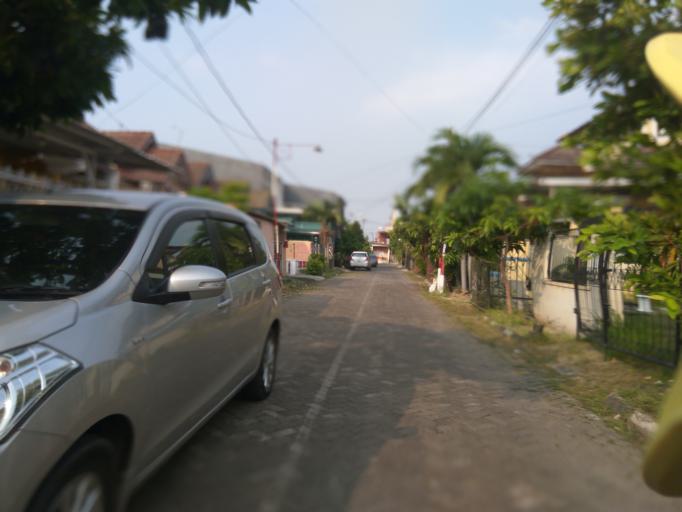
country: ID
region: Central Java
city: Semarang
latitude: -6.9681
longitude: 110.3982
